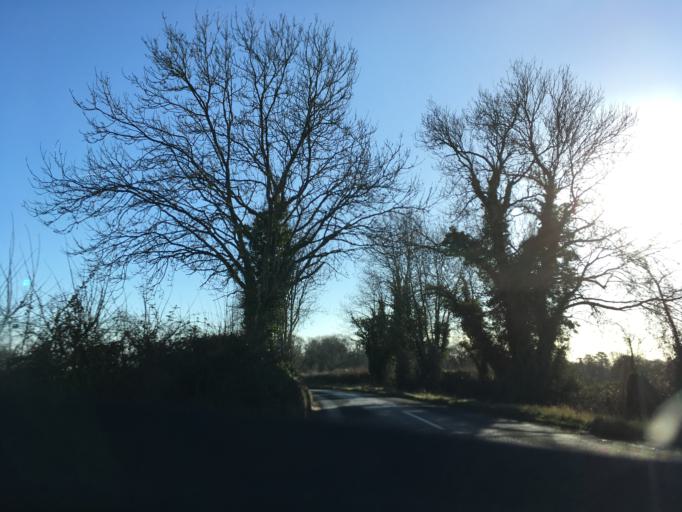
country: GB
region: England
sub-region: Wiltshire
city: Nettleton
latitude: 51.5078
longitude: -2.2319
